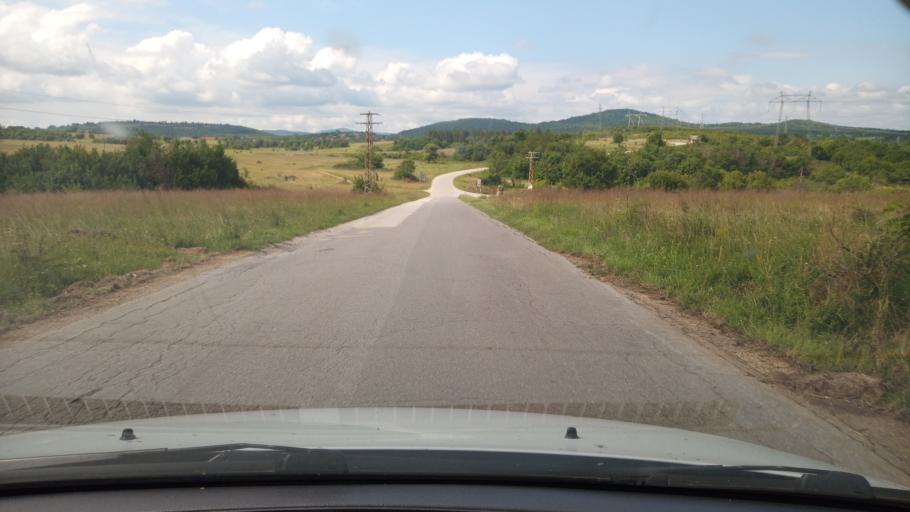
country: BG
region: Pleven
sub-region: Obshtina Cherven Bryag
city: Cherven Bryag
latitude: 43.1806
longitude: 24.0799
